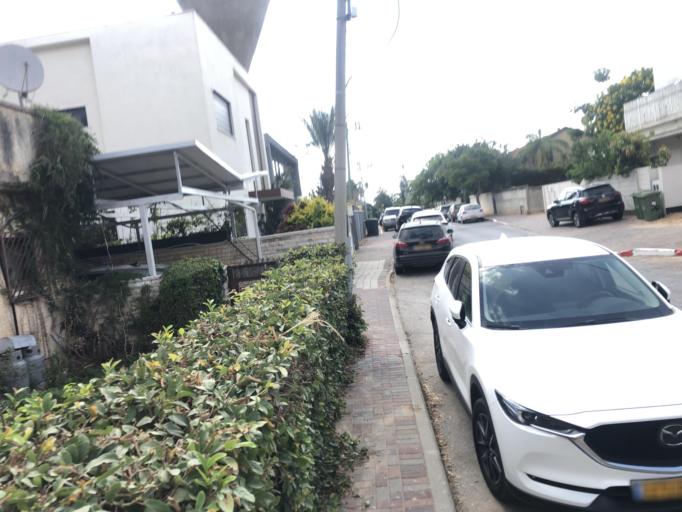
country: IL
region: Central District
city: Yehud
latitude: 32.0401
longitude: 34.8871
